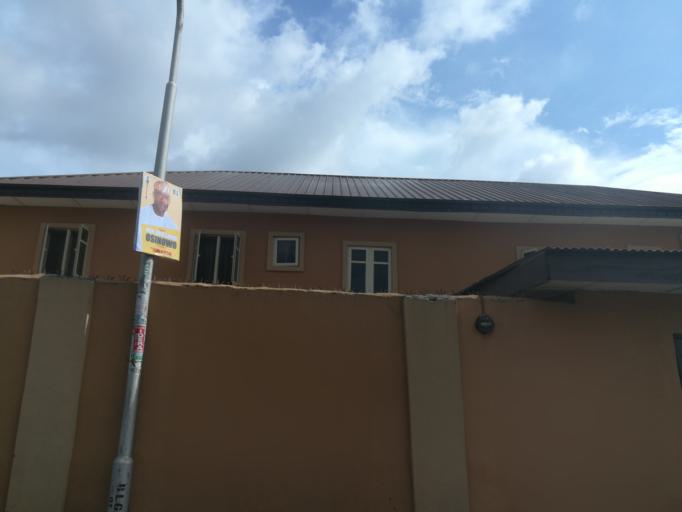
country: NG
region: Lagos
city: Somolu
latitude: 6.5450
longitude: 3.3743
